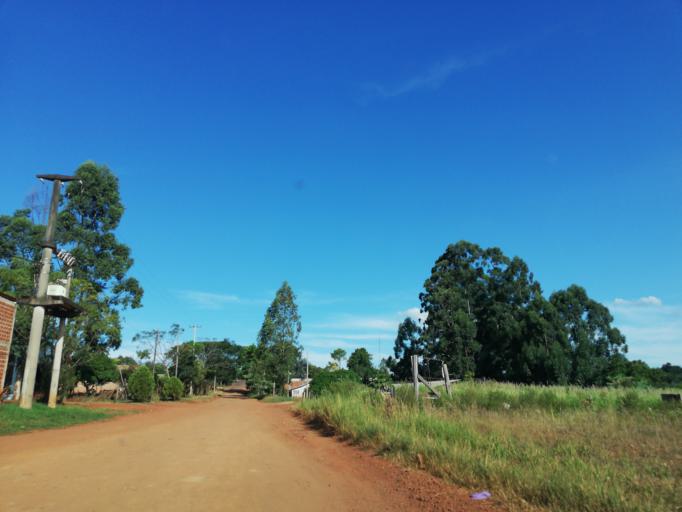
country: AR
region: Misiones
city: Dos de Mayo
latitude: -26.9916
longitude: -54.4963
